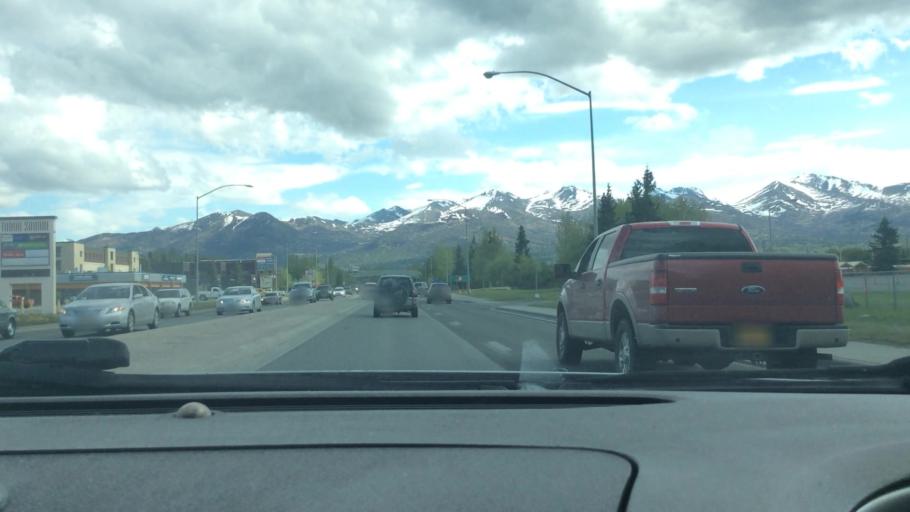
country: US
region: Alaska
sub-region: Anchorage Municipality
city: Anchorage
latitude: 61.1808
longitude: -149.8168
